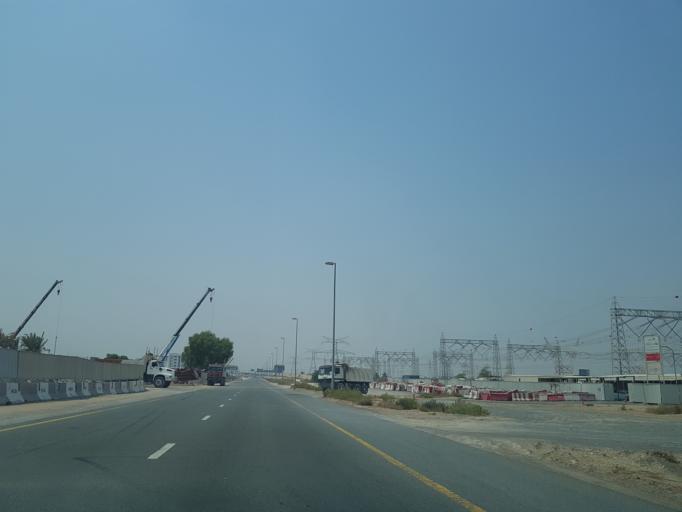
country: AE
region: Ash Shariqah
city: Sharjah
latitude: 25.2270
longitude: 55.4096
